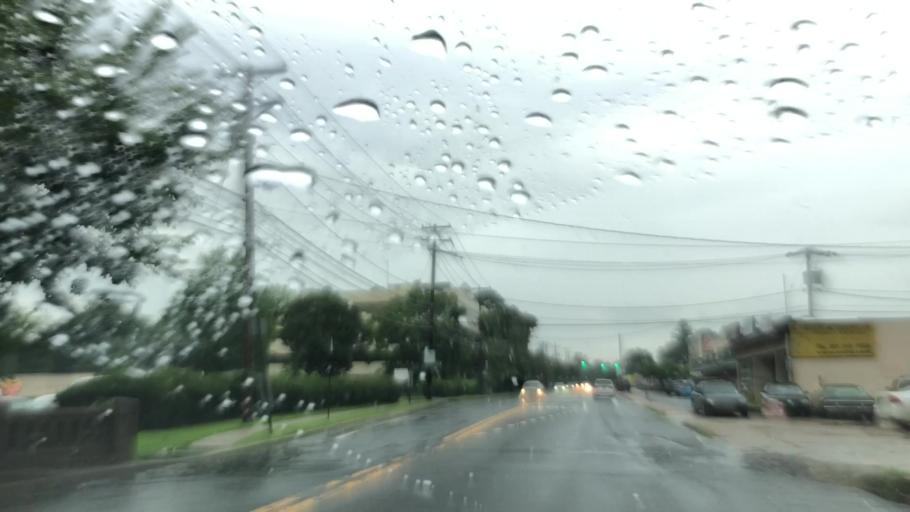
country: US
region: New Jersey
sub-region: Bergen County
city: Rochelle Park
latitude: 40.9129
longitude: -74.0788
